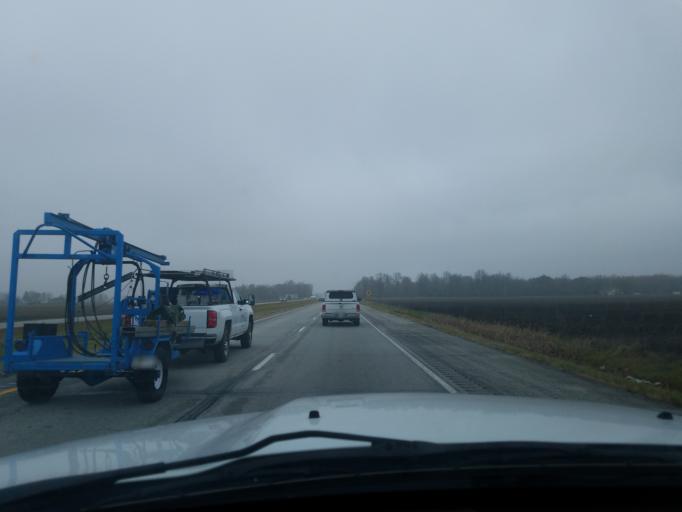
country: US
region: Indiana
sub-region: Tipton County
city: Tipton
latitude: 40.2471
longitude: -86.1274
